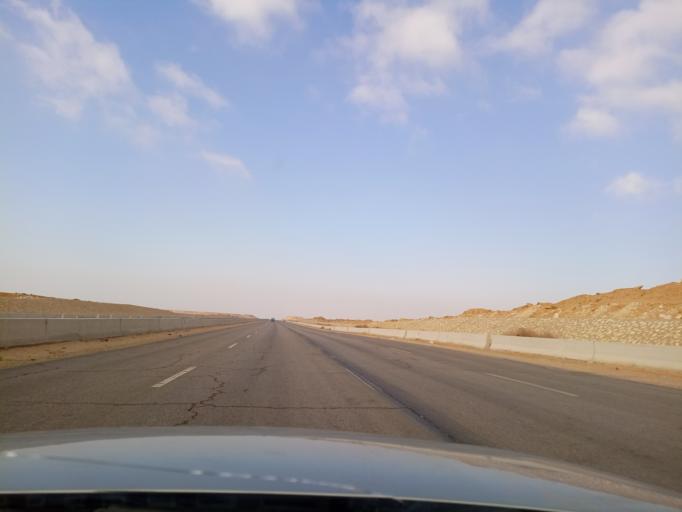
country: EG
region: Al Jizah
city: Al `Ayyat
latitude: 29.6689
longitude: 31.1852
